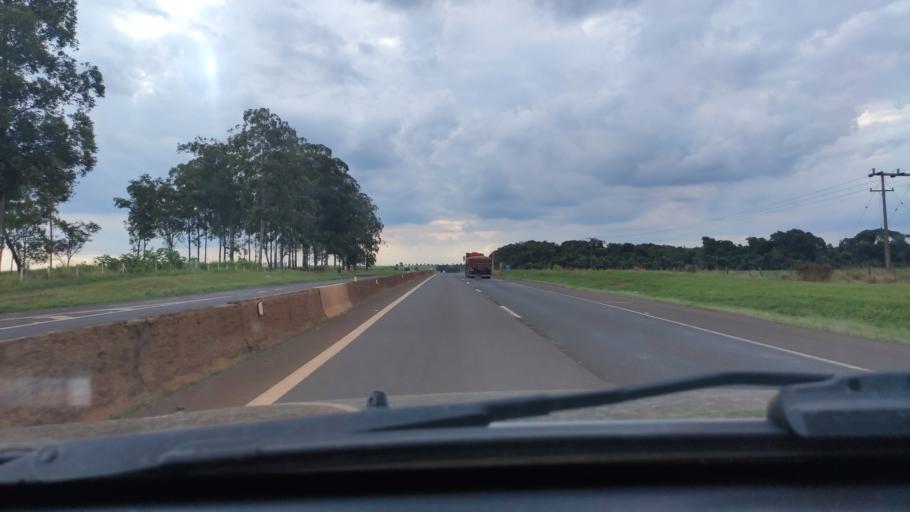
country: BR
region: Sao Paulo
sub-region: Palmital
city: Palmital
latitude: -22.8347
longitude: -50.0227
